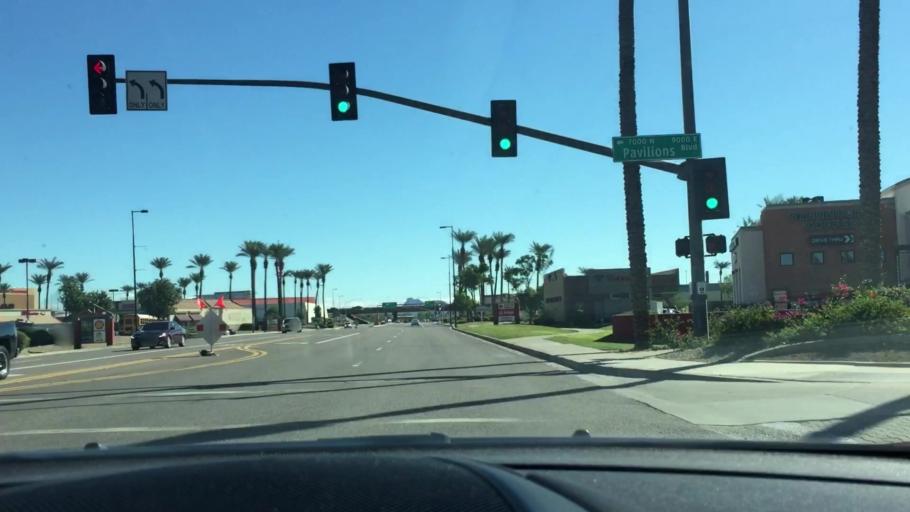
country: US
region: Arizona
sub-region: Maricopa County
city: Scottsdale
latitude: 33.5384
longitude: -111.8867
